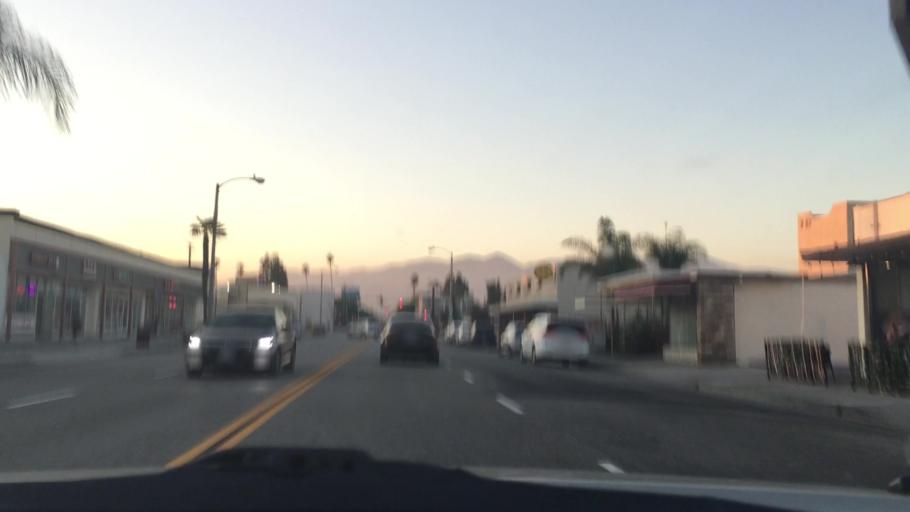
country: US
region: California
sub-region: Los Angeles County
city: Monterey Park
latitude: 34.0605
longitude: -118.1228
